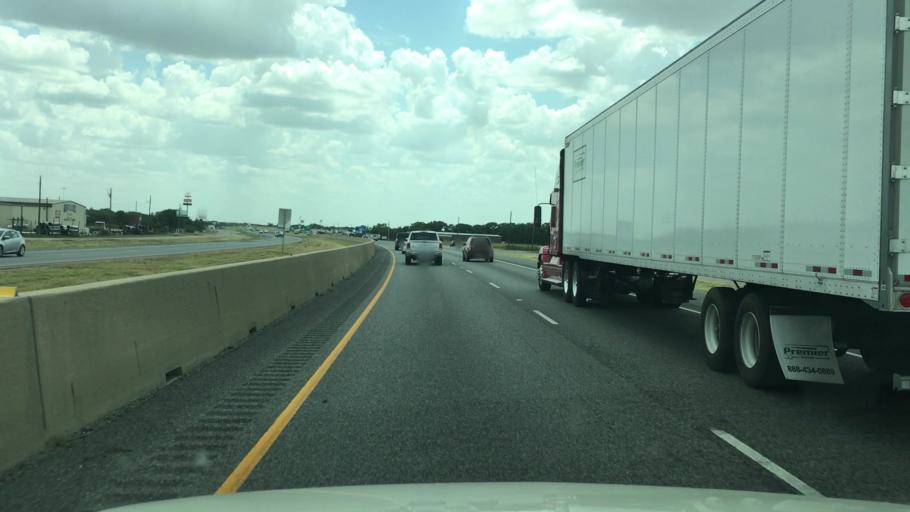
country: US
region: Texas
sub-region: Hunt County
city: Caddo Mills
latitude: 33.0513
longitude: -96.1727
